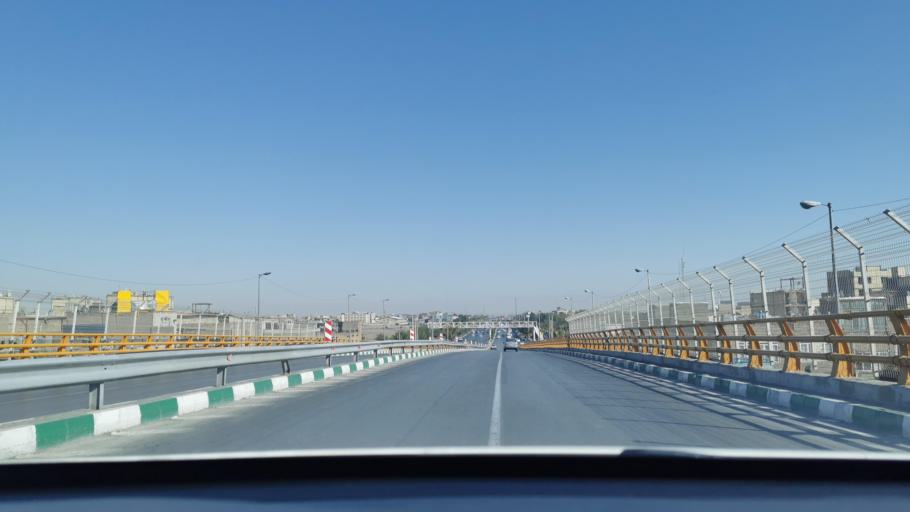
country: IR
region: Razavi Khorasan
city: Mashhad
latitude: 36.3286
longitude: 59.6243
